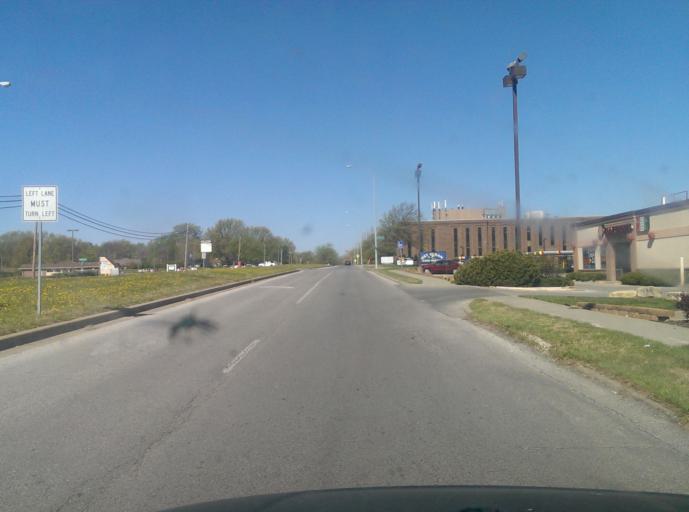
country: US
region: Kansas
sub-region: Johnson County
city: Leawood
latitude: 38.9260
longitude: -94.5850
